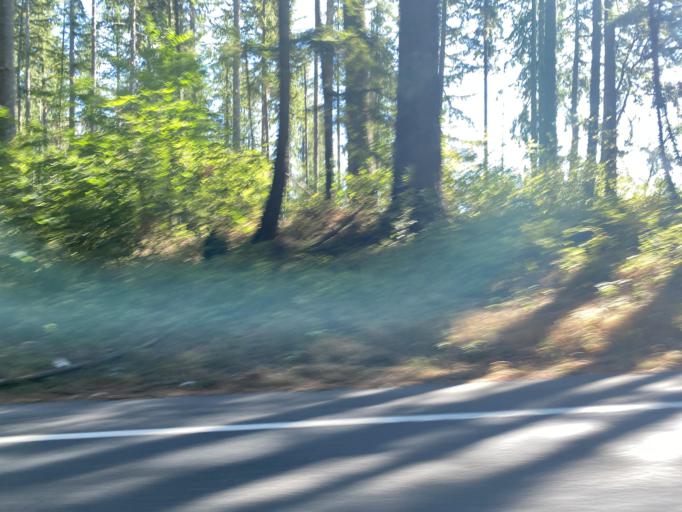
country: US
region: Washington
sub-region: Thurston County
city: Rainier
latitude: 46.9093
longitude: -122.7330
